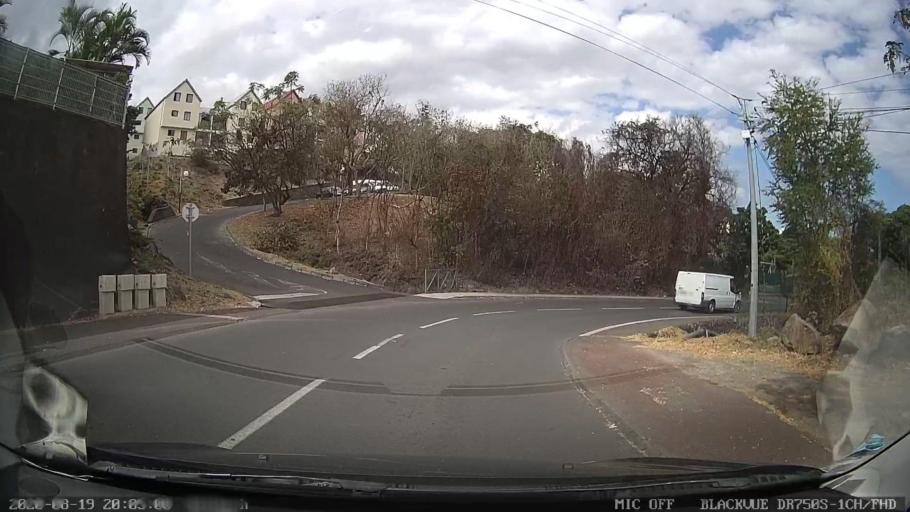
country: RE
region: Reunion
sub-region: Reunion
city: La Possession
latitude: -20.9536
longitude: 55.3402
